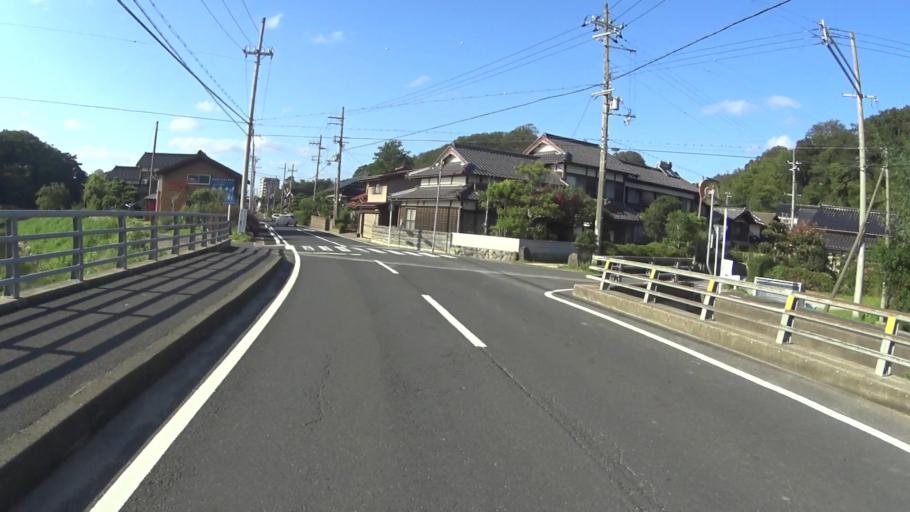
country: JP
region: Hyogo
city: Toyooka
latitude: 35.6534
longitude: 134.9697
